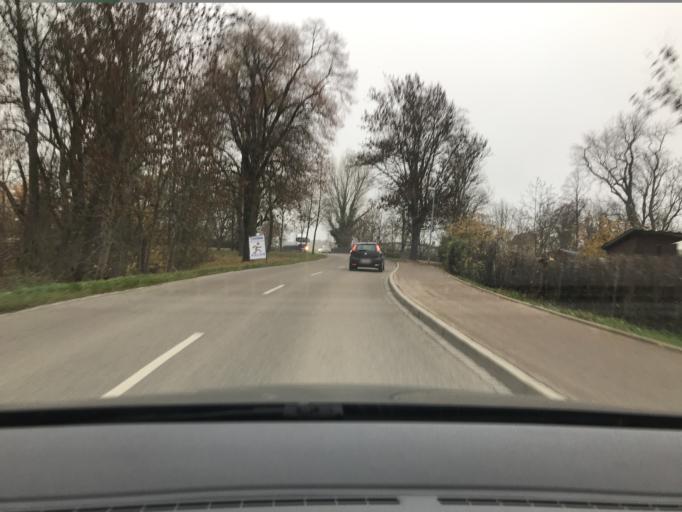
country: DE
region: Bavaria
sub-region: Swabia
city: Noerdlingen
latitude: 48.8497
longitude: 10.4781
